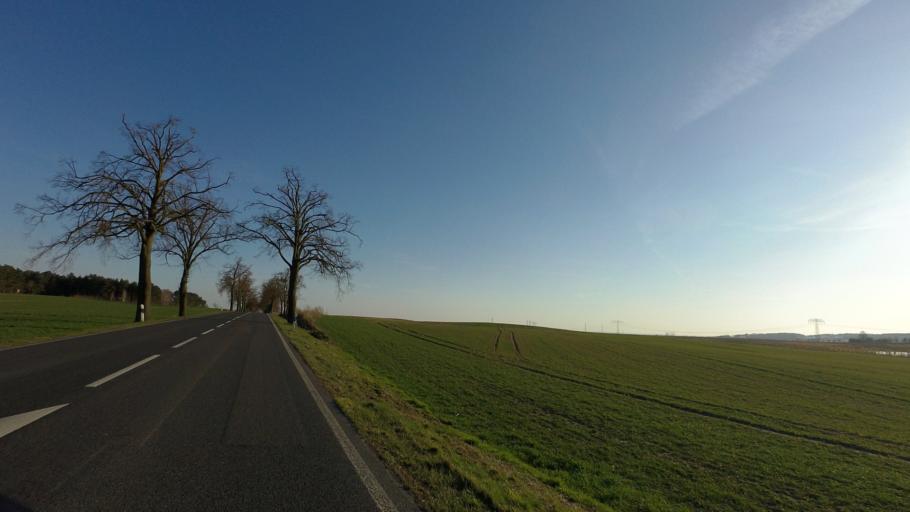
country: DE
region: Brandenburg
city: Britz
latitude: 52.9050
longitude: 13.8022
